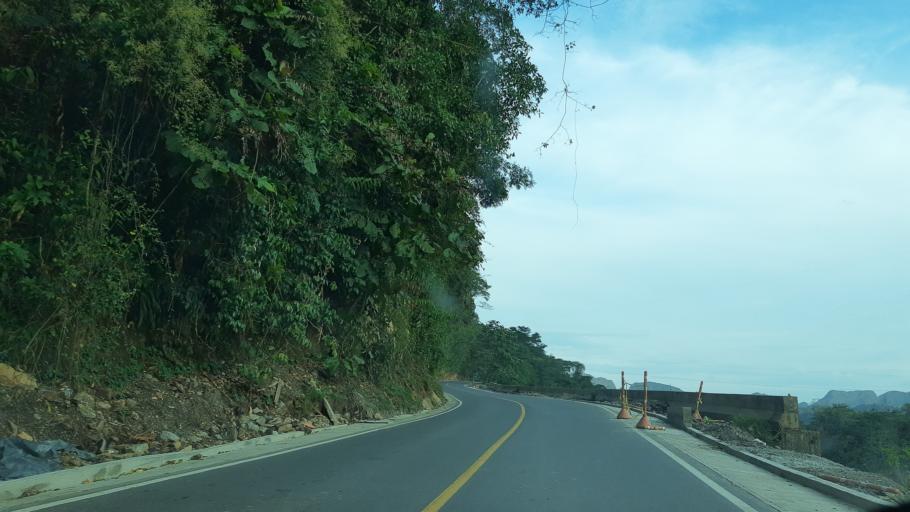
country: CO
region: Boyaca
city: San Luis de Gaceno
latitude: 4.8302
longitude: -73.2062
